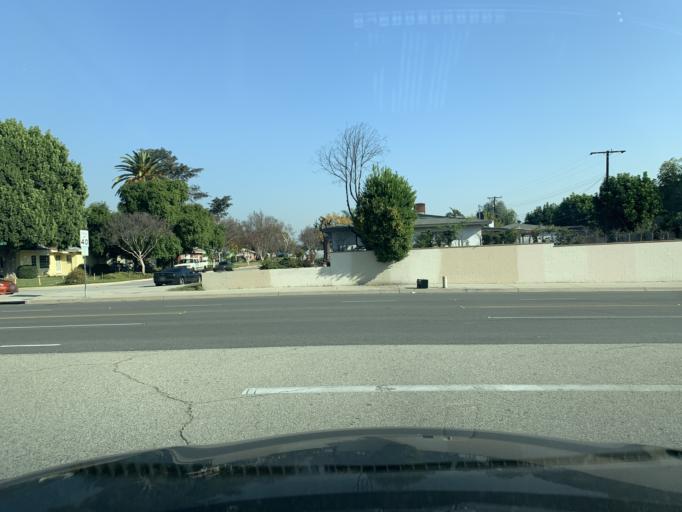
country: US
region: California
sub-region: Los Angeles County
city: Covina
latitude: 34.0739
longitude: -117.8991
